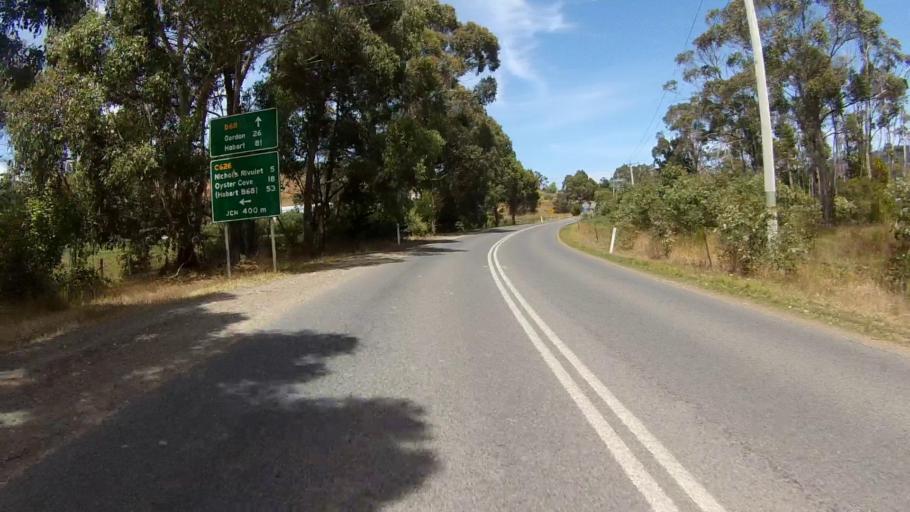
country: AU
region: Tasmania
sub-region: Huon Valley
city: Cygnet
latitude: -43.1693
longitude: 147.0959
